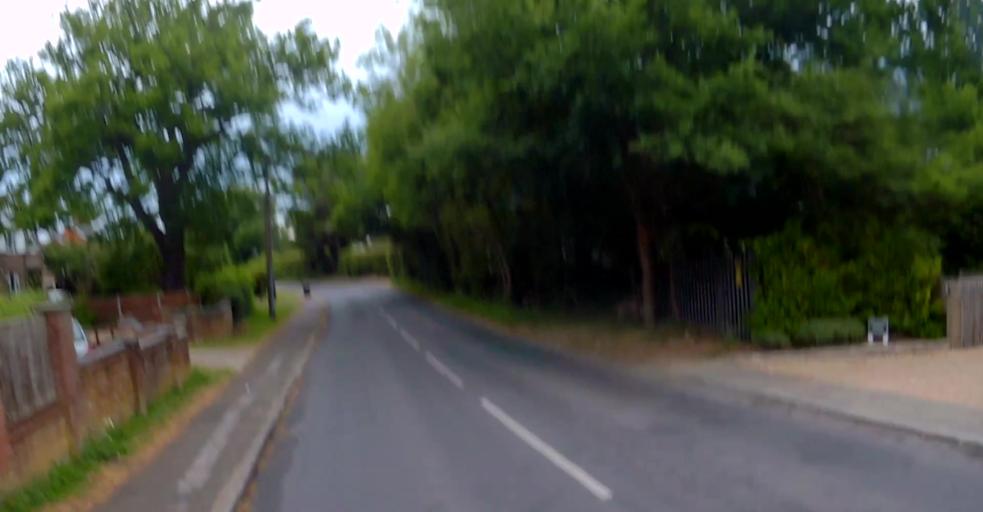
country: GB
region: England
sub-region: Hampshire
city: Fleet
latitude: 51.2649
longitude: -0.8548
